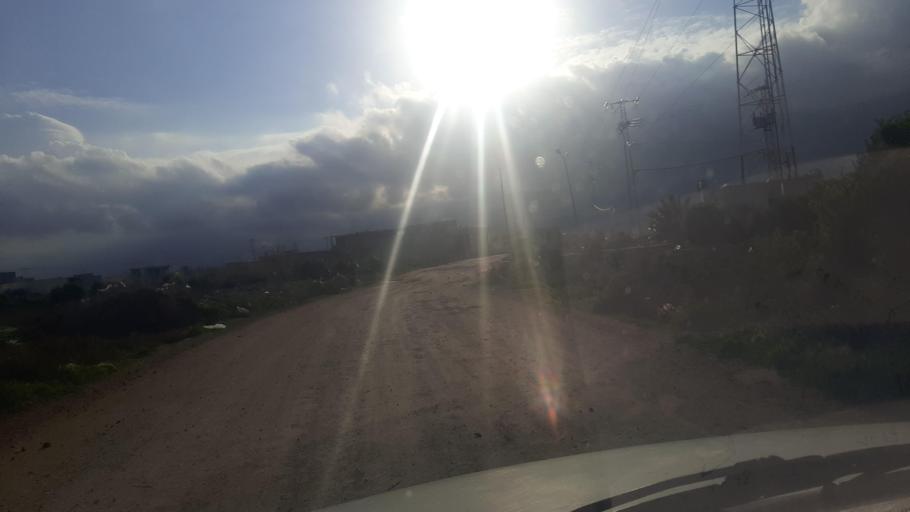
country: TN
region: Nabul
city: Manzil Bu Zalafah
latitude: 36.7120
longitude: 10.4851
